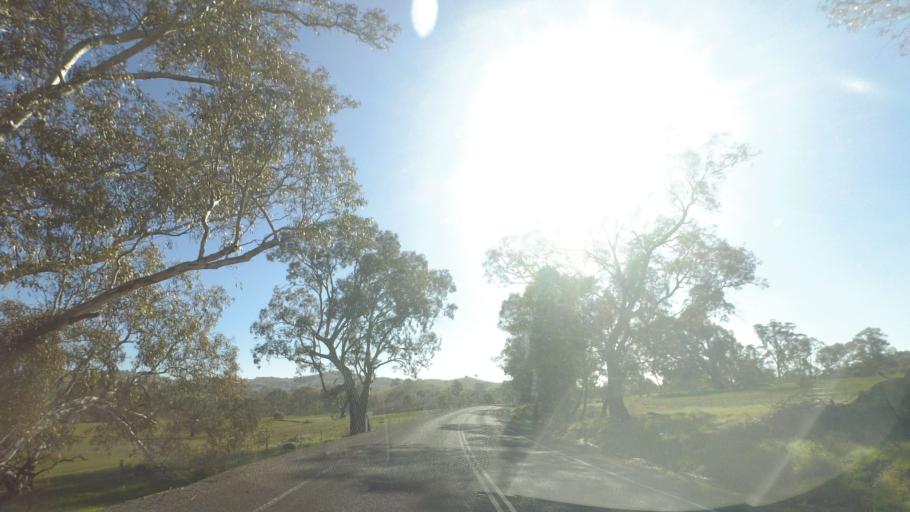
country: AU
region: Victoria
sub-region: Mount Alexander
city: Castlemaine
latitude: -36.9503
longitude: 144.3395
